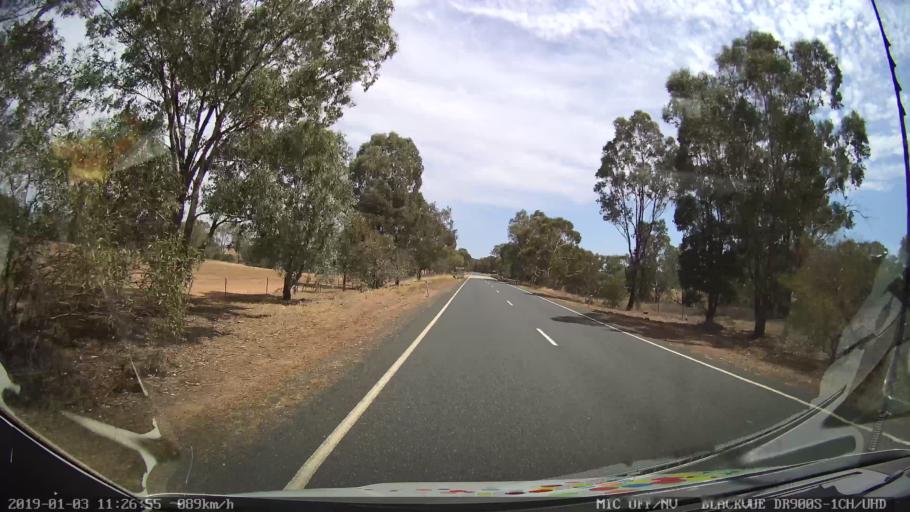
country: AU
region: New South Wales
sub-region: Weddin
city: Grenfell
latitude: -34.0189
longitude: 148.2223
